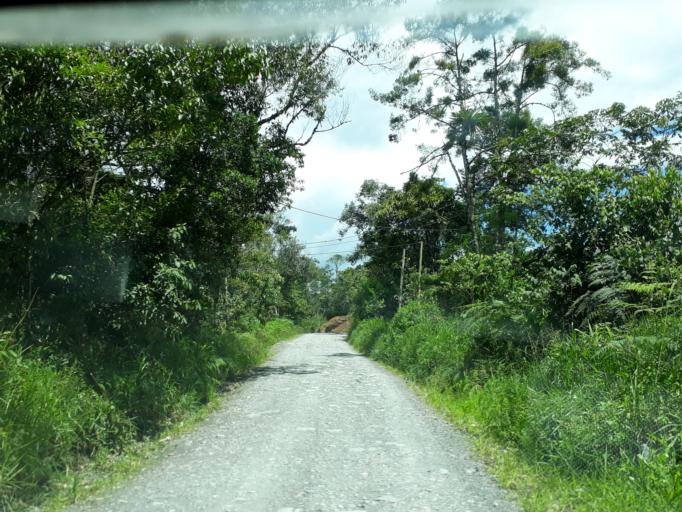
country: CO
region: Cundinamarca
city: Topaipi
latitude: 5.3611
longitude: -74.1980
